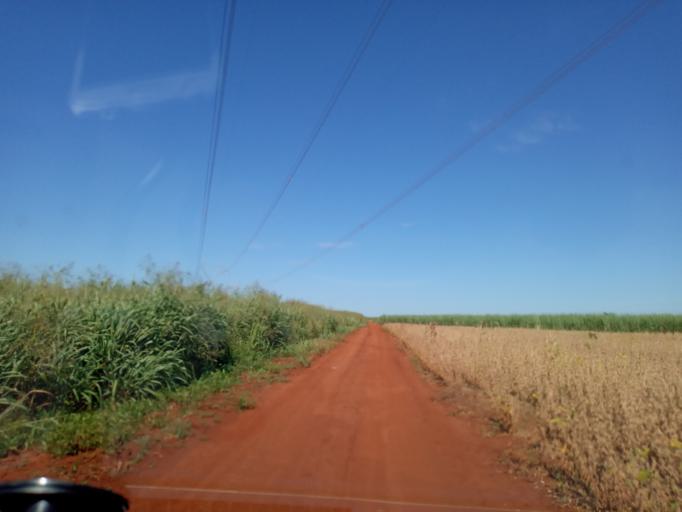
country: BR
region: Goias
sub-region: Itumbiara
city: Itumbiara
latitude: -18.4542
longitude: -49.1469
